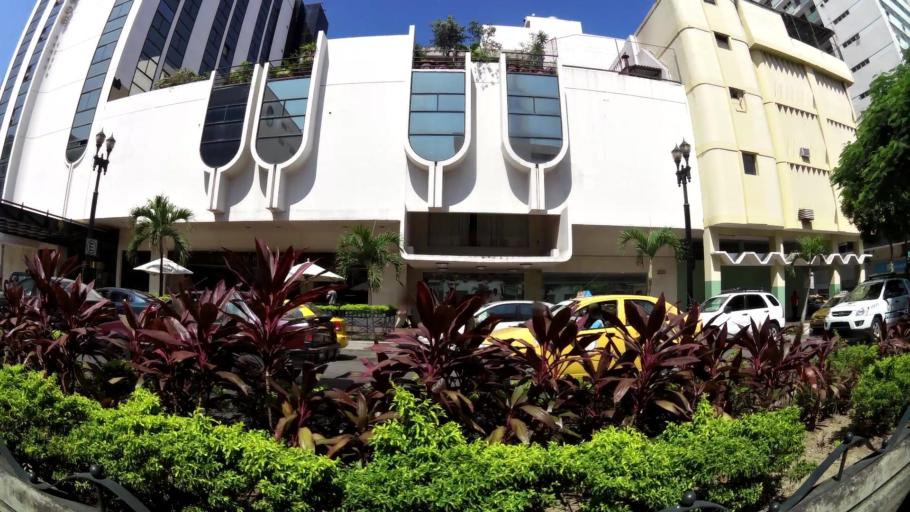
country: EC
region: Guayas
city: Guayaquil
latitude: -2.1885
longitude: -79.8917
